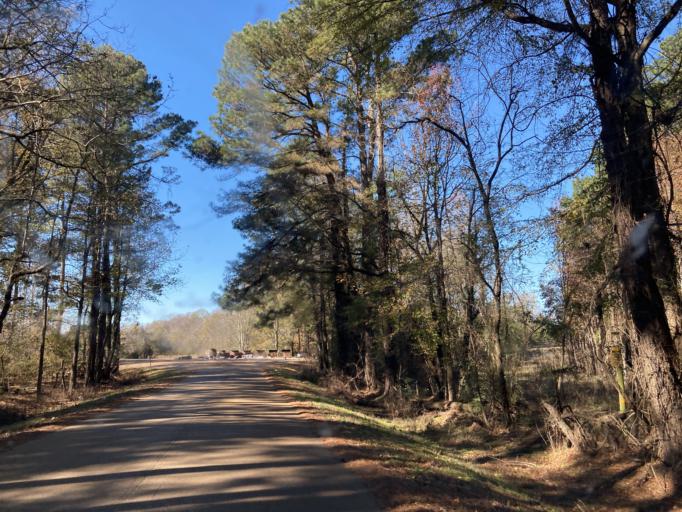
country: US
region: Mississippi
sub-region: Hinds County
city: Lynchburg
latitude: 32.5815
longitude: -90.5683
